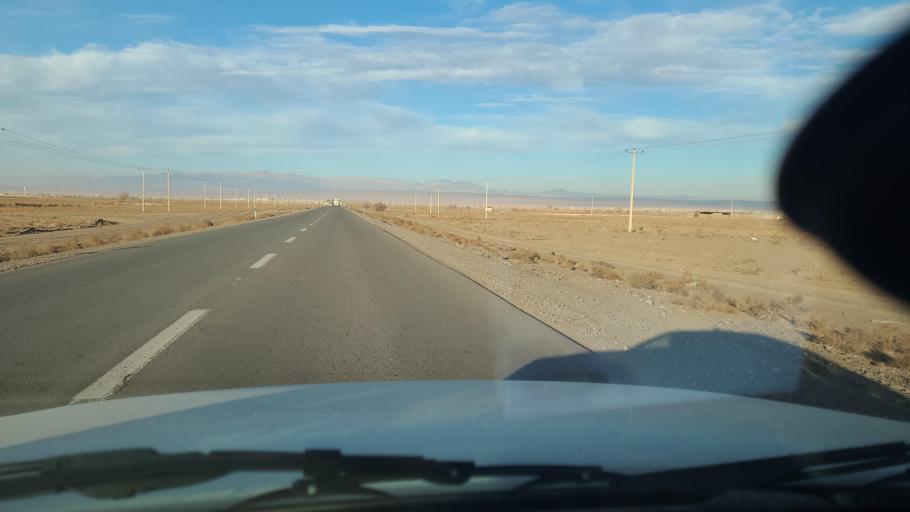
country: IR
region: Razavi Khorasan
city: Neqab
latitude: 36.5930
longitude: 57.5857
